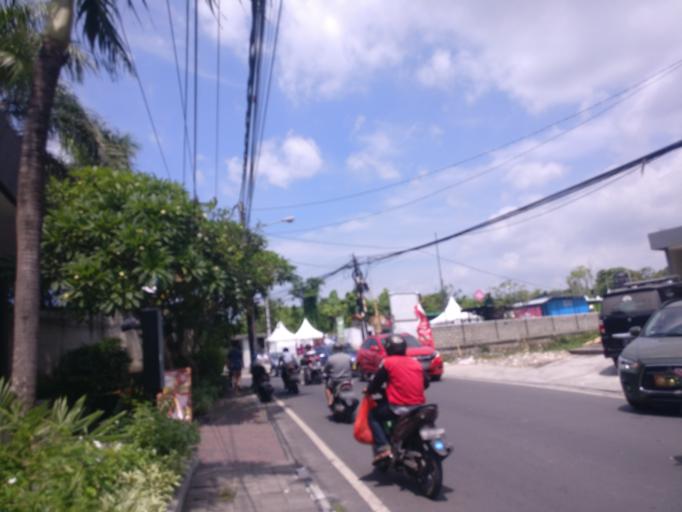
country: ID
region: Bali
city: Kuta
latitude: -8.6764
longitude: 115.1587
